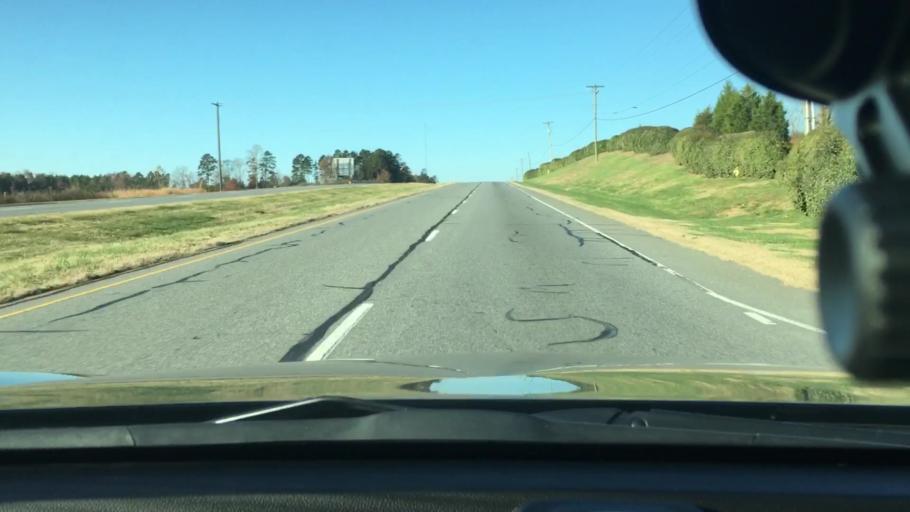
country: US
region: North Carolina
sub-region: Cabarrus County
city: Concord
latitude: 35.3702
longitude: -80.5663
